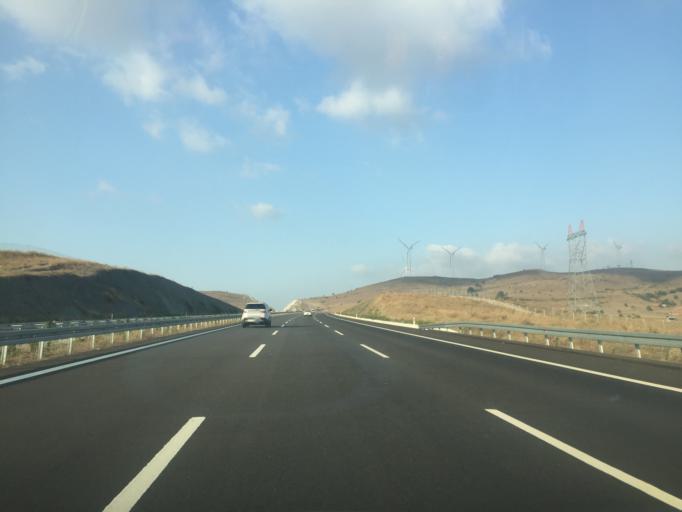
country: TR
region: Balikesir
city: Balikesir
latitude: 39.6967
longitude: 27.7776
